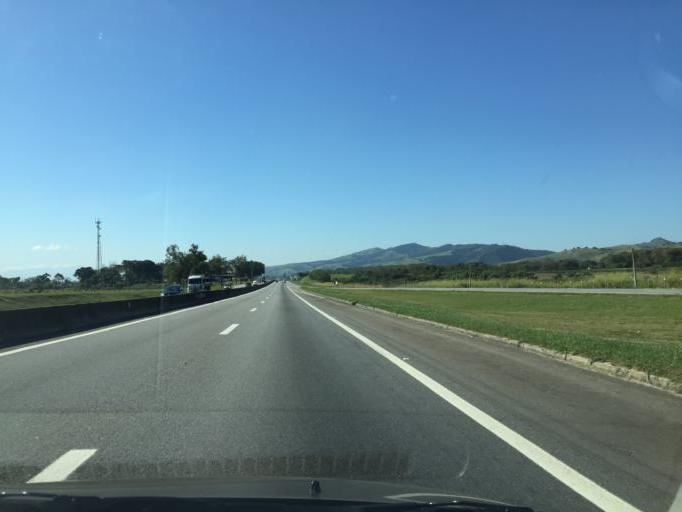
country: BR
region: Sao Paulo
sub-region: Pindamonhangaba
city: Pindamonhangaba
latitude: -22.9217
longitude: -45.3439
